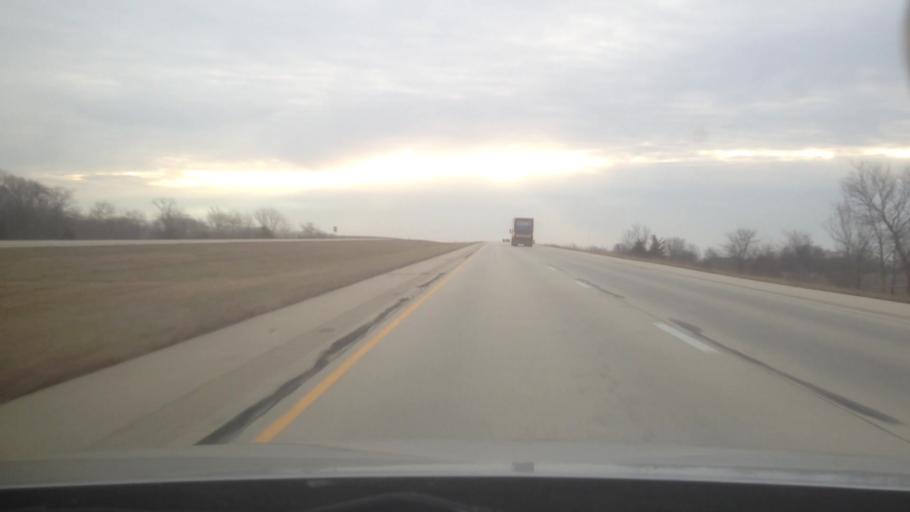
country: US
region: Illinois
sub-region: Macon County
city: Decatur
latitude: 39.8035
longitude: -89.0139
